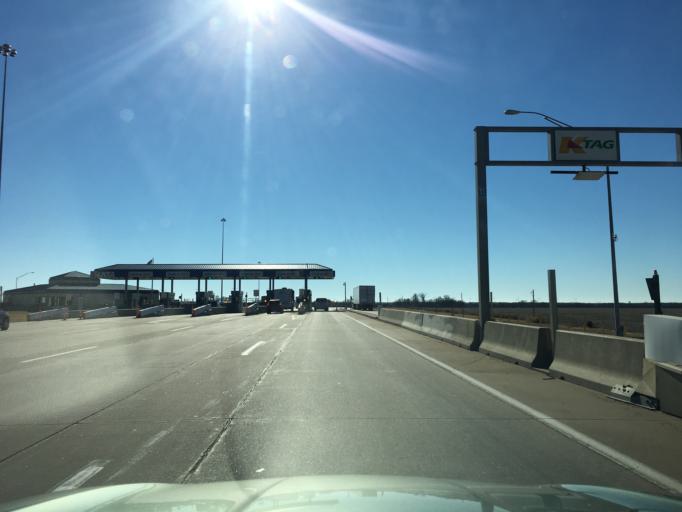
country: US
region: Kansas
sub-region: Sumner County
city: Wellington
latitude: 37.2401
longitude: -97.3393
